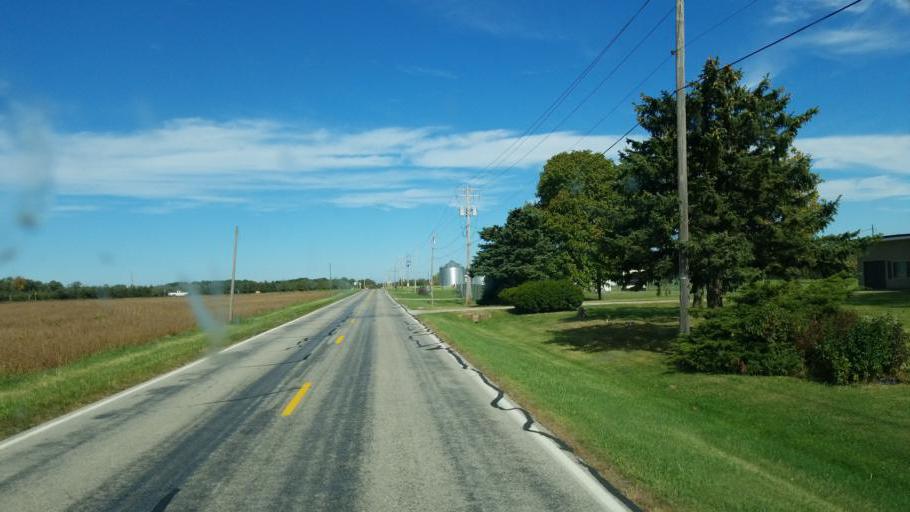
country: US
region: Ohio
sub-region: Huron County
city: Wakeman
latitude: 41.2995
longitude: -82.4927
